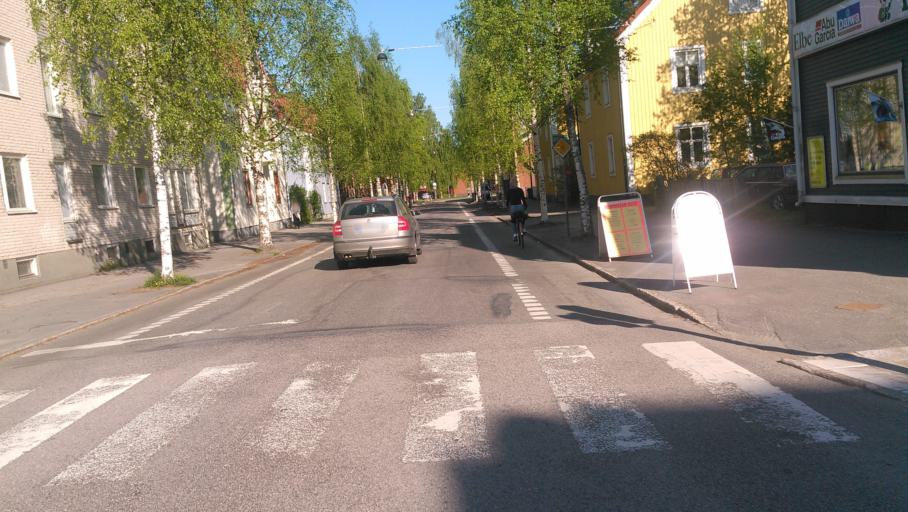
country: SE
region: Vaesterbotten
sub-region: Umea Kommun
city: Umea
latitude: 63.8227
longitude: 20.2814
